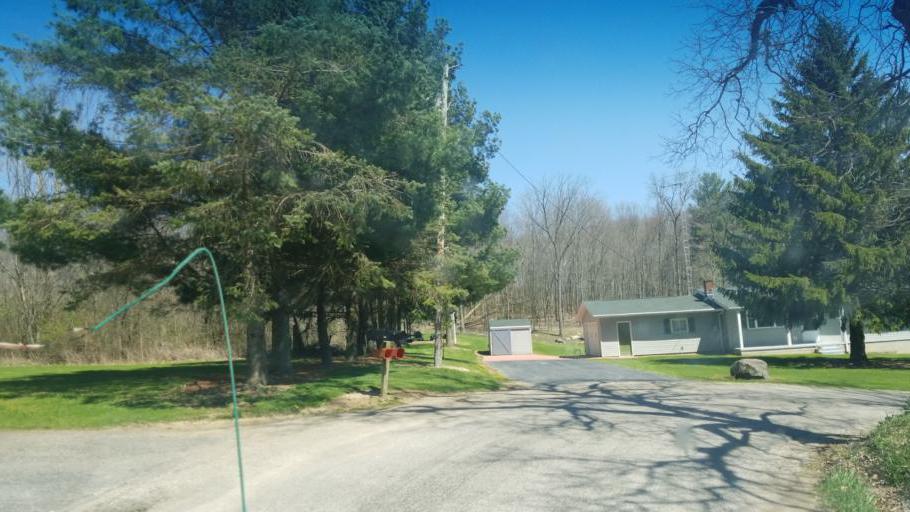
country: US
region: Ohio
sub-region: Ashland County
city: Ashland
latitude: 40.8438
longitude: -82.3868
